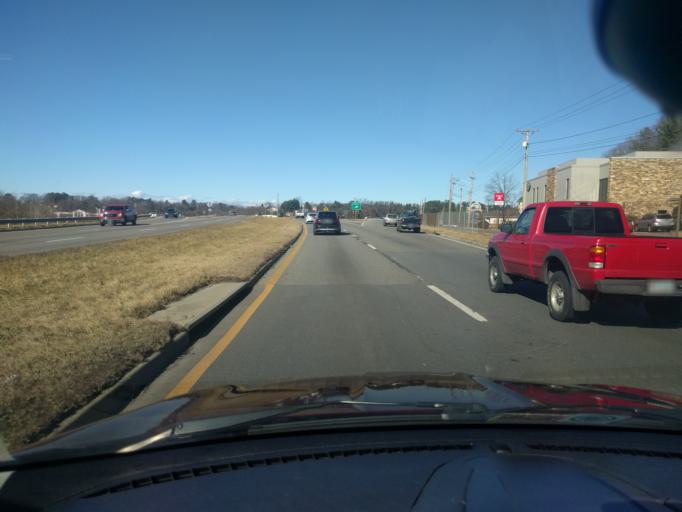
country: US
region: Virginia
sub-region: Roanoke County
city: Narrows
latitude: 37.2295
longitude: -79.9712
